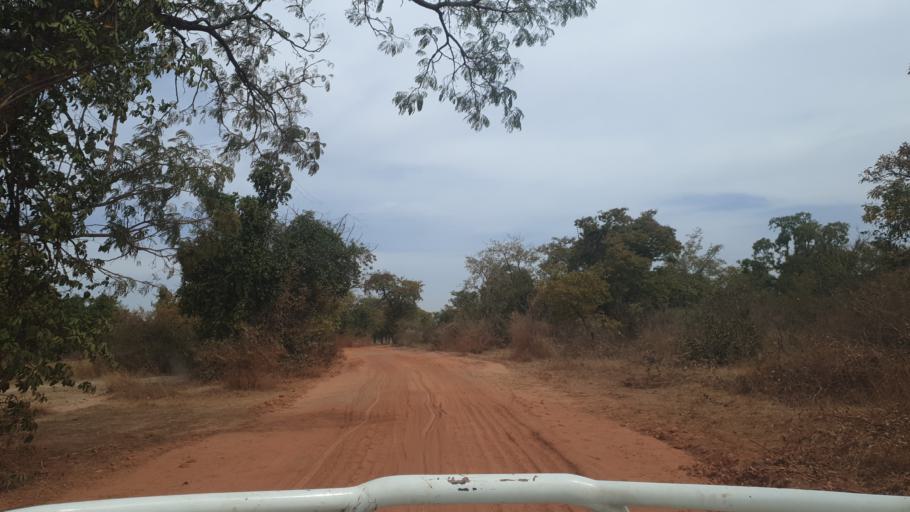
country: ML
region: Sikasso
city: Yorosso
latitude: 12.2260
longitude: -4.7513
